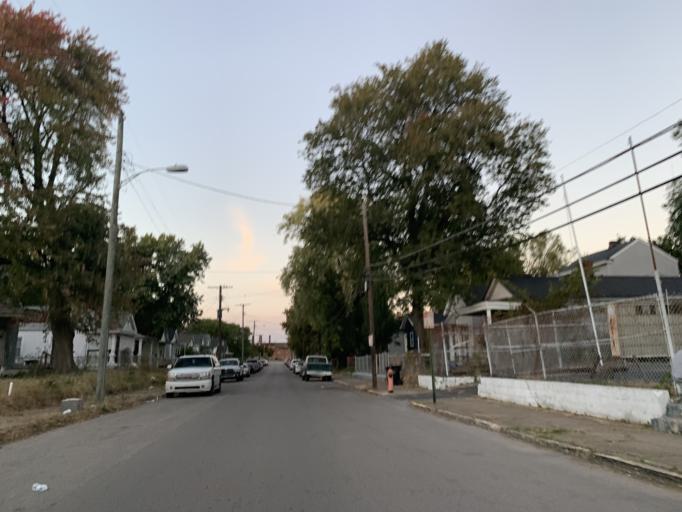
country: US
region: Kentucky
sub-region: Jefferson County
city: Louisville
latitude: 38.2276
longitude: -85.7701
